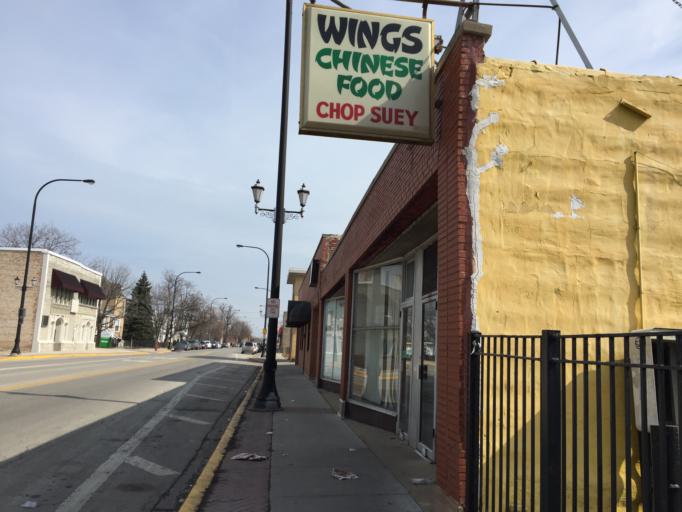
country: US
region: Illinois
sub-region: Cook County
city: Cicero
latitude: 41.8456
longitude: -87.7537
